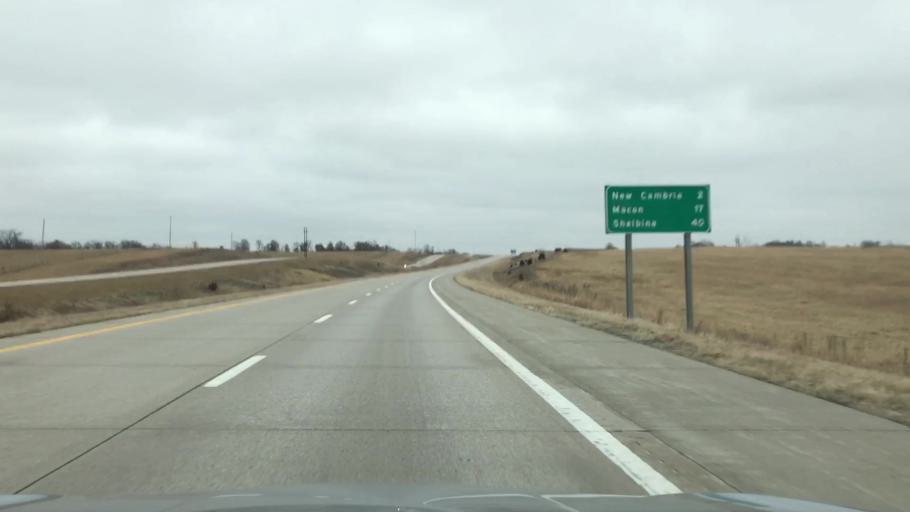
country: US
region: Missouri
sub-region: Linn County
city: Marceline
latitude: 39.7647
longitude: -92.7864
